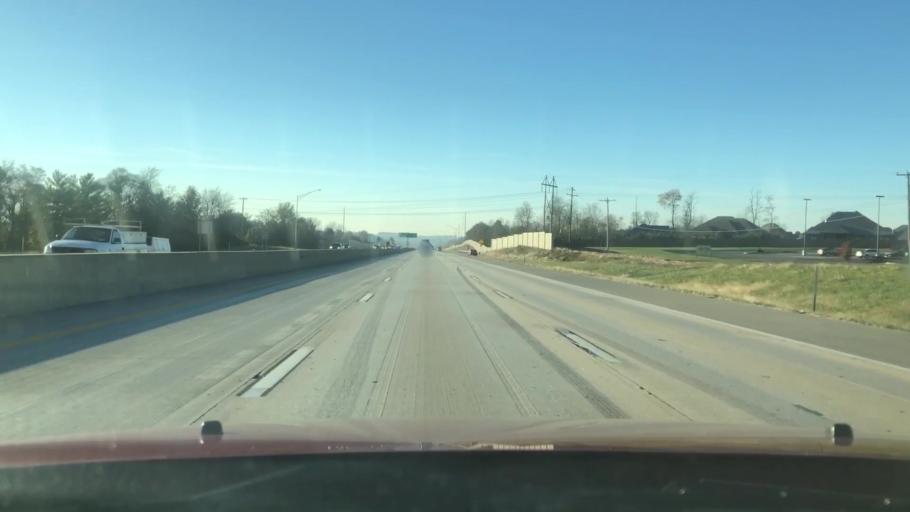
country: US
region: Missouri
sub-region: Greene County
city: Springfield
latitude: 37.1561
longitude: -93.2246
